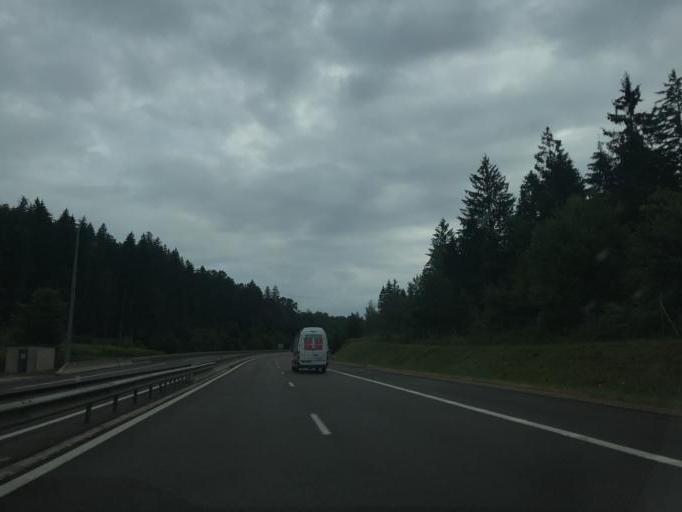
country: FR
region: Rhone-Alpes
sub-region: Departement de l'Ain
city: Bellignat
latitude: 46.2484
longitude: 5.6242
